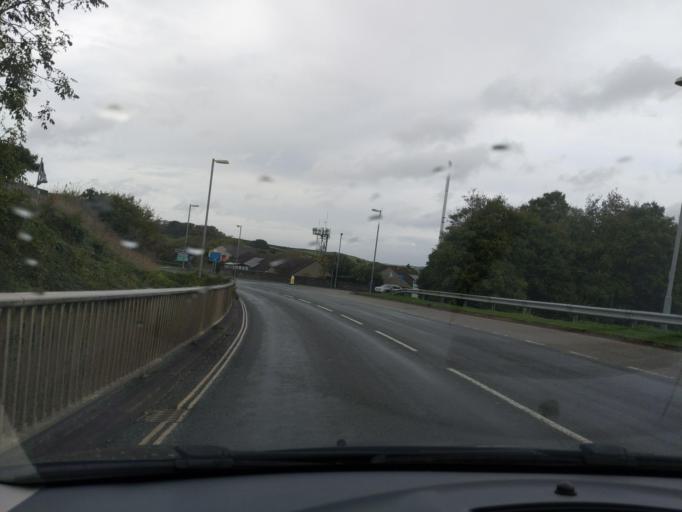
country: GB
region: England
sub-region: Cornwall
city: Padstow
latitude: 50.5381
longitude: -4.9412
